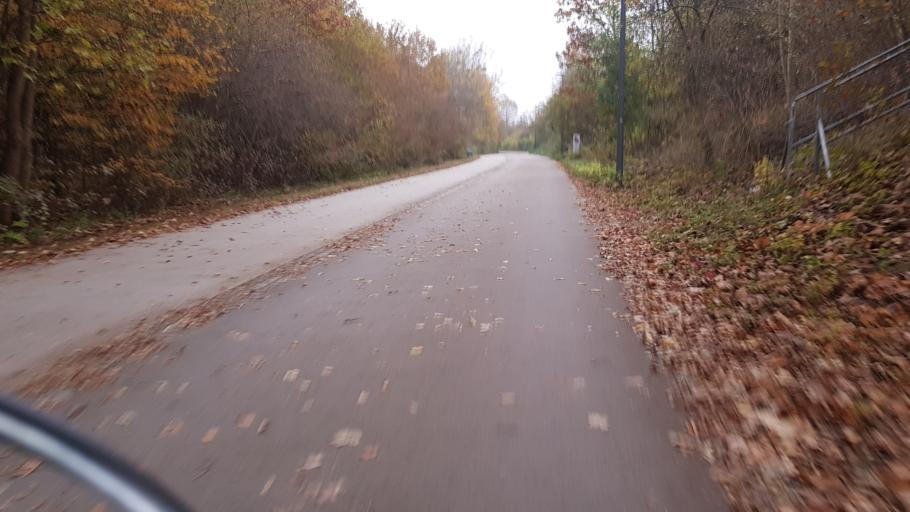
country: DE
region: Bavaria
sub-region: Upper Bavaria
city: Pasing
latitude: 48.1528
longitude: 11.4839
